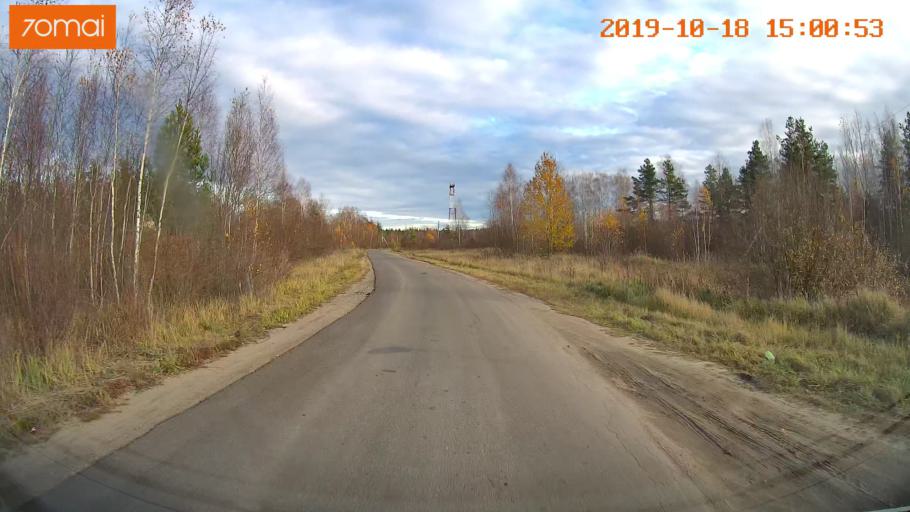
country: RU
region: Vladimir
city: Kurlovo
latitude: 55.5000
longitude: 40.5914
